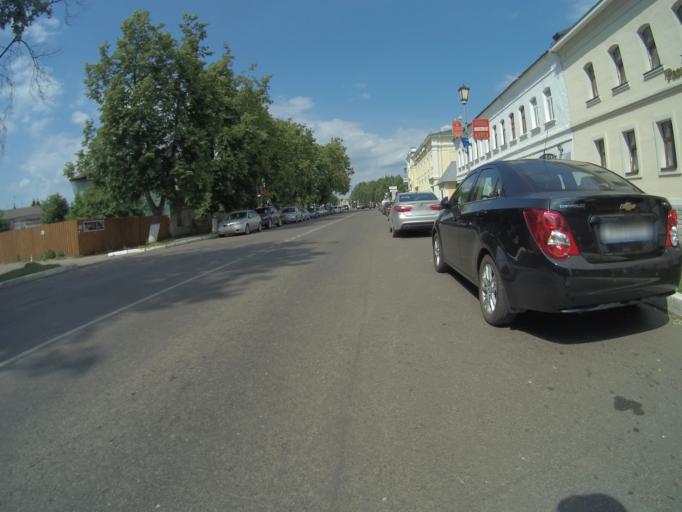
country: RU
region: Vladimir
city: Suzdal'
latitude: 56.4180
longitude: 40.4490
